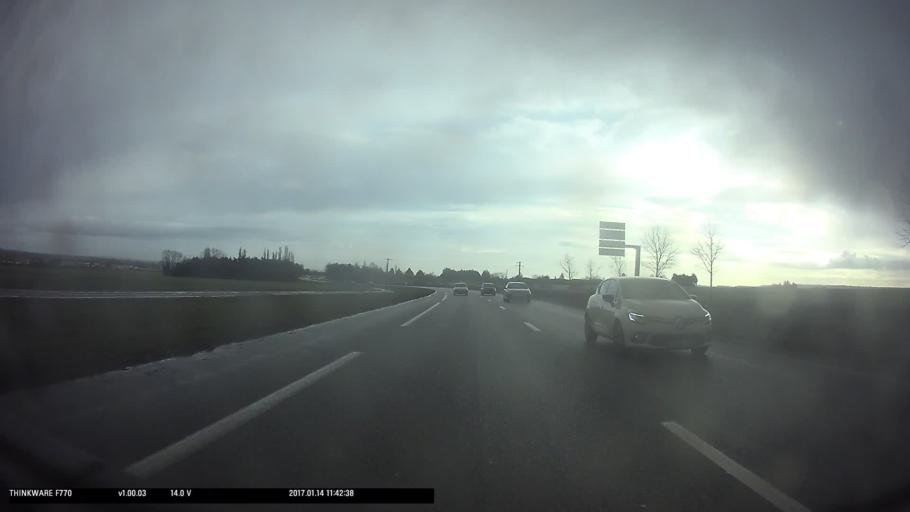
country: FR
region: Ile-de-France
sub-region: Departement du Val-d'Oise
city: Sagy
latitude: 49.0724
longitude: 1.9568
